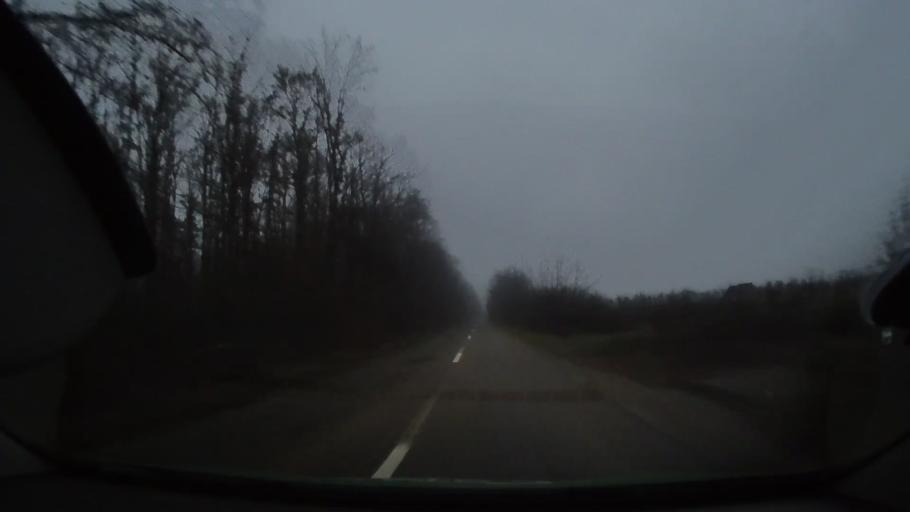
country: RO
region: Arad
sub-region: Comuna Beliu
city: Beliu
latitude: 46.4844
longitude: 22.0044
